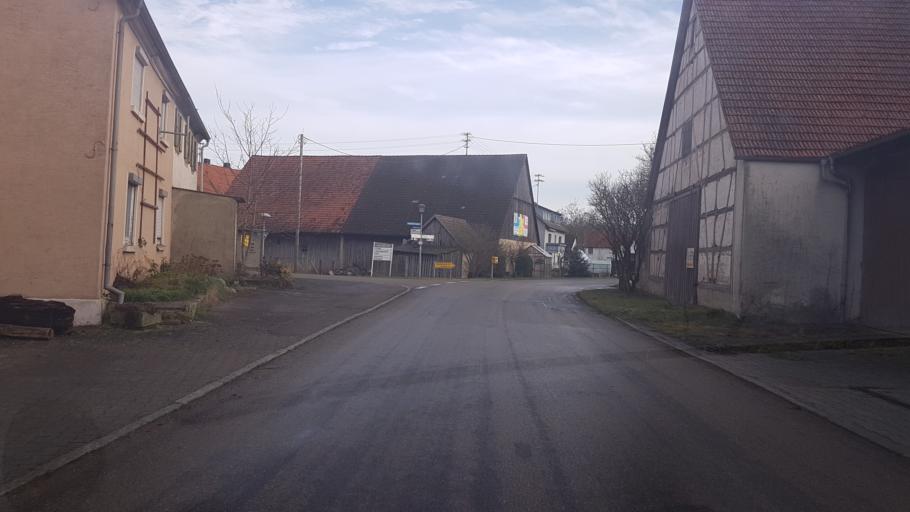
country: DE
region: Baden-Wuerttemberg
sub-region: Regierungsbezirk Stuttgart
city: Wallhausen
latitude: 49.2320
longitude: 10.0625
